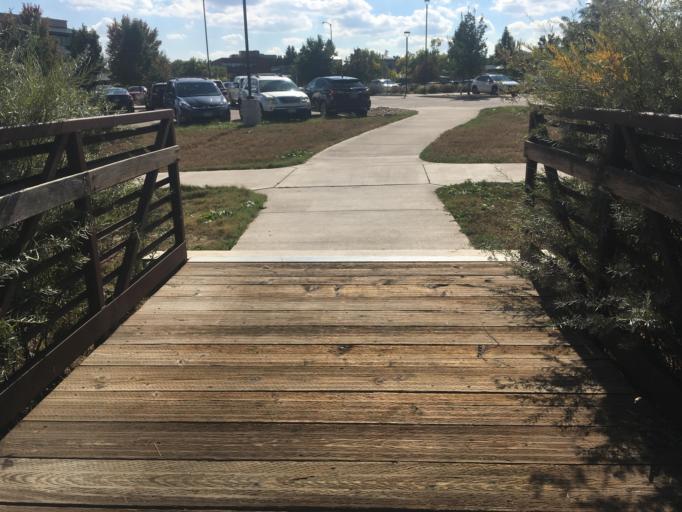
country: US
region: Colorado
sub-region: Broomfield County
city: Broomfield
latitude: 39.9168
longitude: -105.0654
